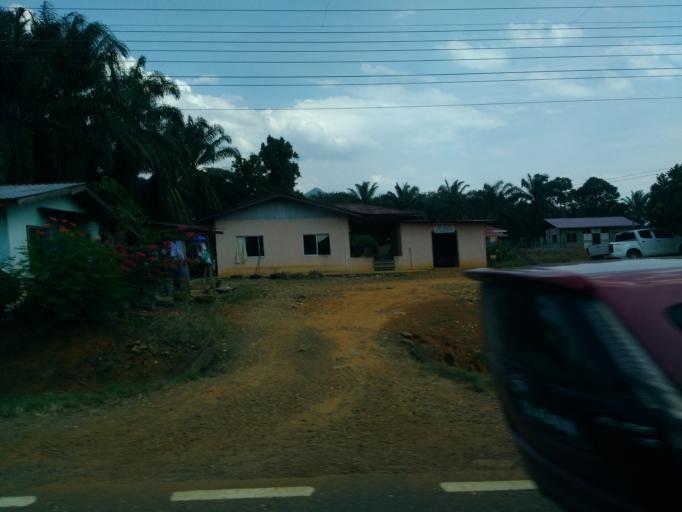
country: MY
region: Sabah
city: Ranau
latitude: 5.6242
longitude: 117.0969
